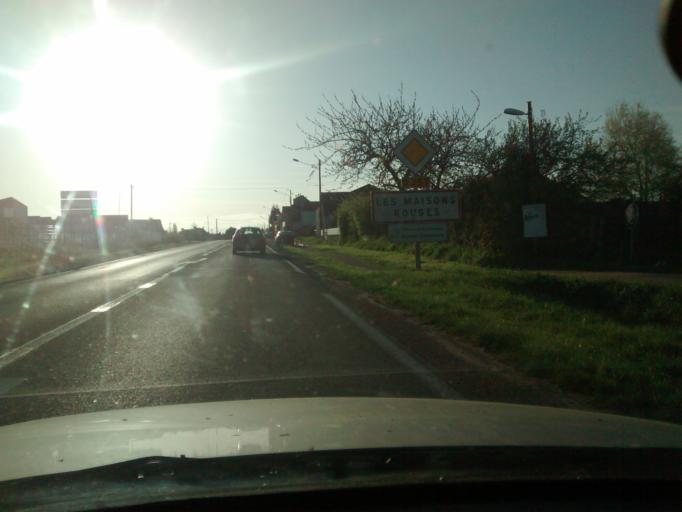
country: FR
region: Pays de la Loire
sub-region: Departement de la Sarthe
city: Trange
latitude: 48.0220
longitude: 0.1015
